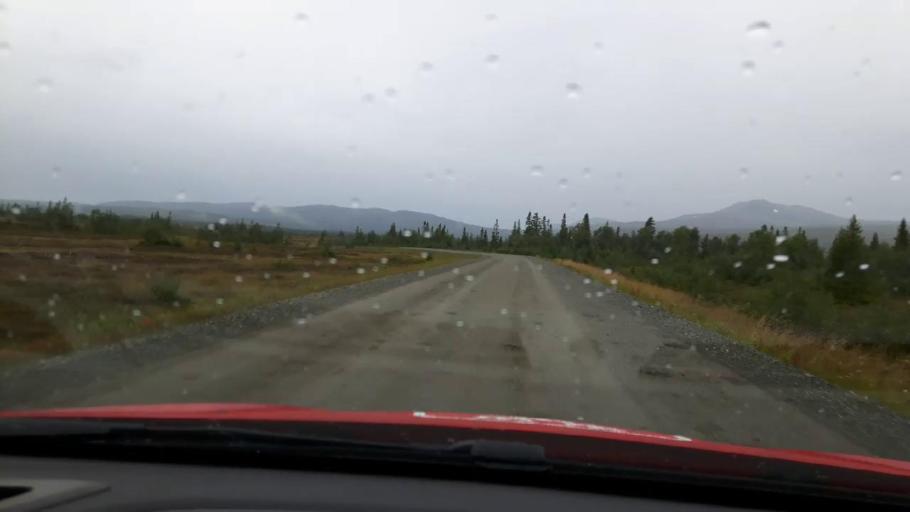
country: NO
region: Nord-Trondelag
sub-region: Meraker
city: Meraker
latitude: 63.5951
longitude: 12.2741
